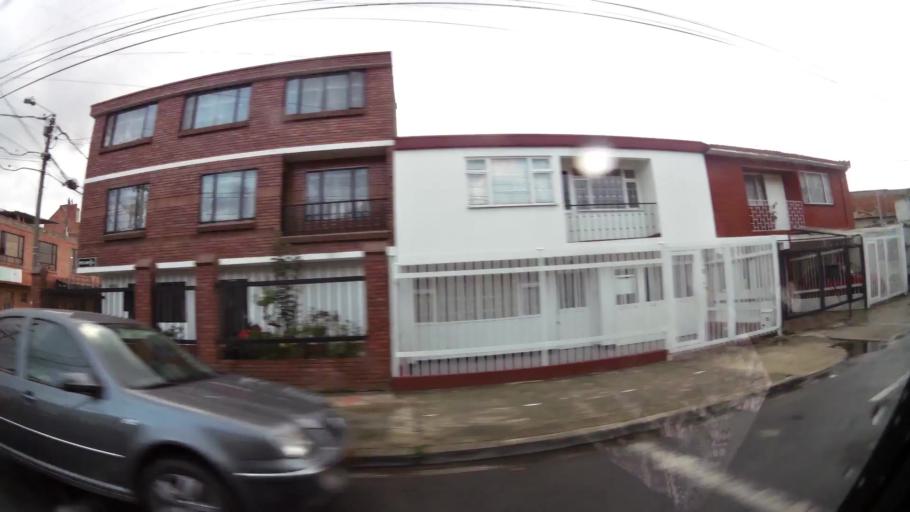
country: CO
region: Cundinamarca
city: Chia
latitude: 4.8650
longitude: -74.0590
